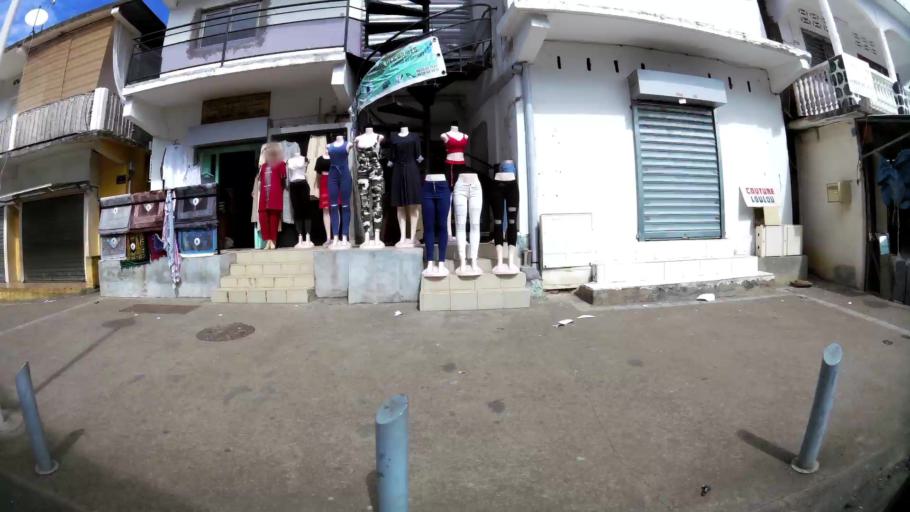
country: YT
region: Mamoudzou
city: Mamoudzou
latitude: -12.7821
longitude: 45.2306
